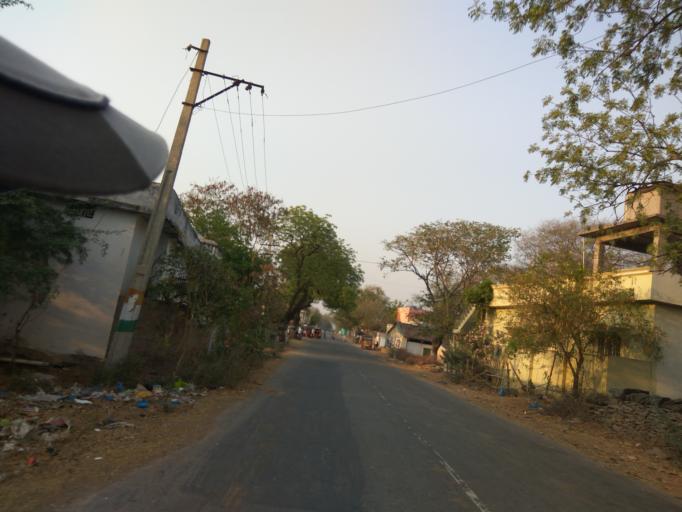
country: IN
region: Andhra Pradesh
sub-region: Prakasam
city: Cumbum
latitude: 15.6389
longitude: 79.1413
